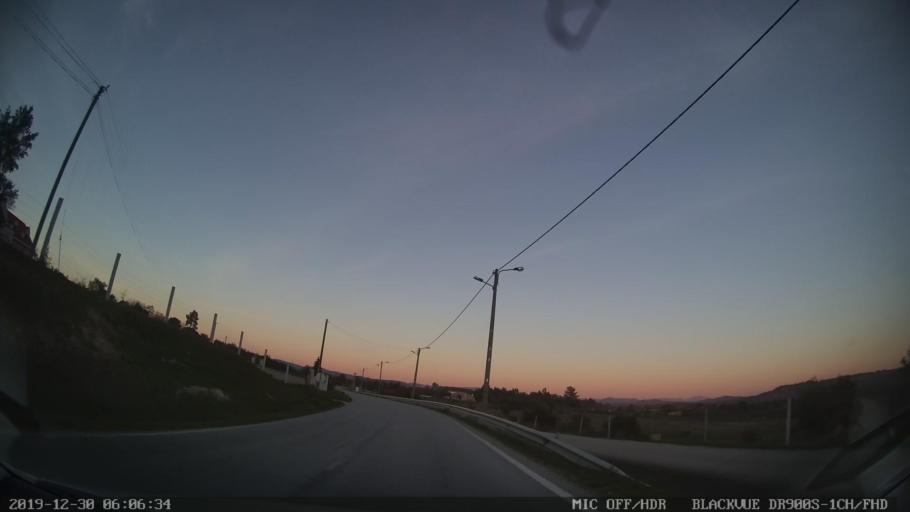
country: PT
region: Castelo Branco
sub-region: Penamacor
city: Penamacor
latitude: 40.0999
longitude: -7.2300
